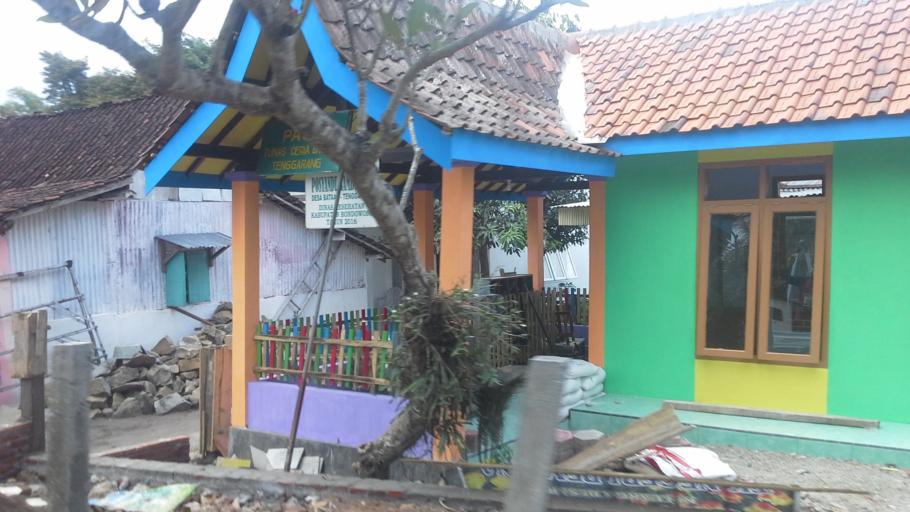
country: ID
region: East Java
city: Bondowoso
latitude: -7.9125
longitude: 113.8456
